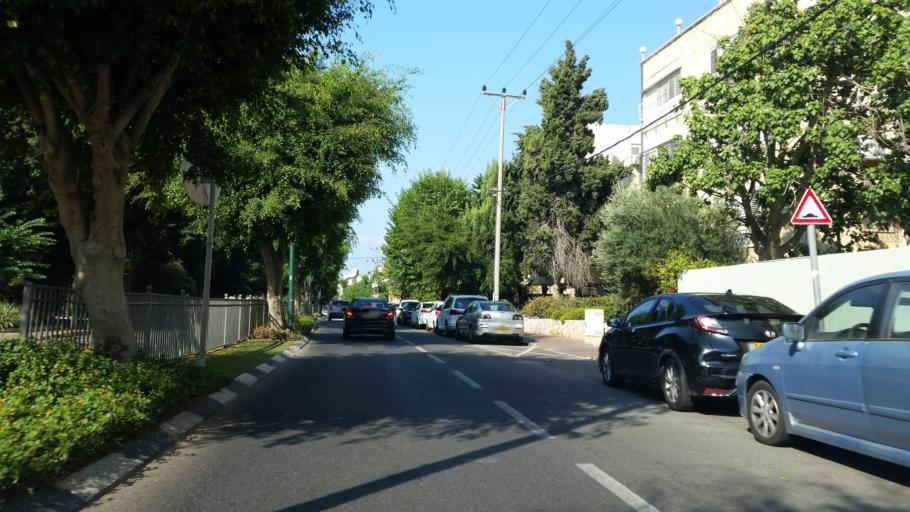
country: IL
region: Tel Aviv
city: Ramat HaSharon
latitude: 32.1615
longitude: 34.8404
